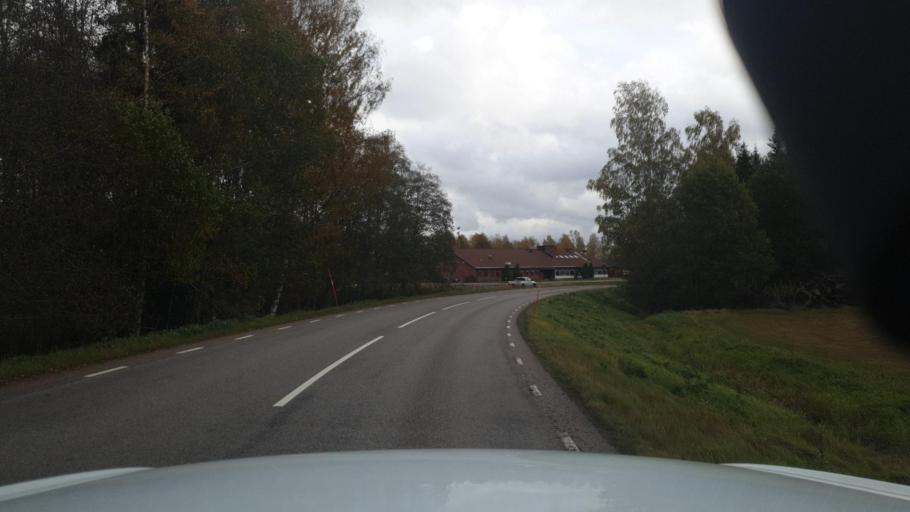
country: SE
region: Vaermland
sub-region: Sunne Kommun
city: Sunne
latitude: 59.7922
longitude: 13.0930
